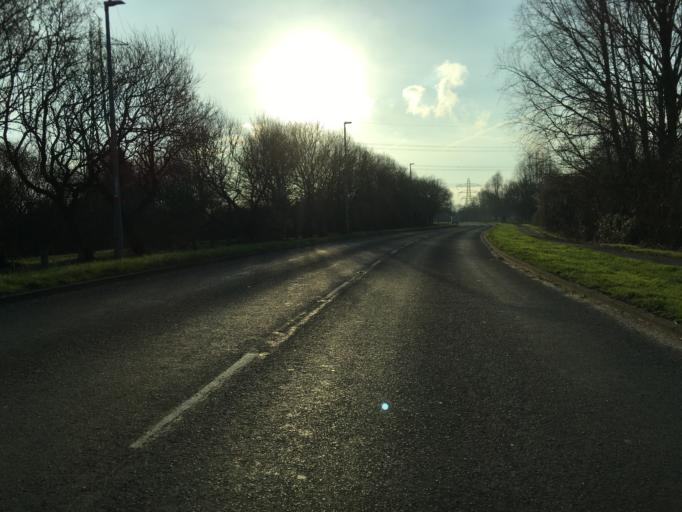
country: GB
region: Wales
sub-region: Newport
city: Nash
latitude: 51.5691
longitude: -2.9424
